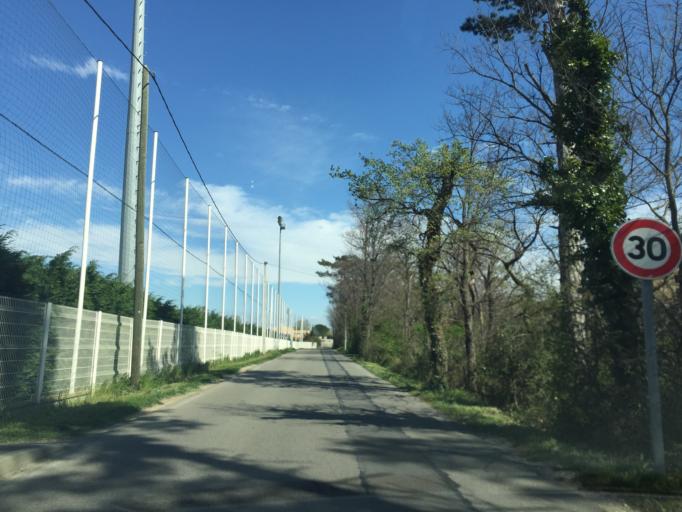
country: FR
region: Provence-Alpes-Cote d'Azur
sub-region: Departement du Vaucluse
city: Sorgues
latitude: 43.9947
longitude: 4.8795
